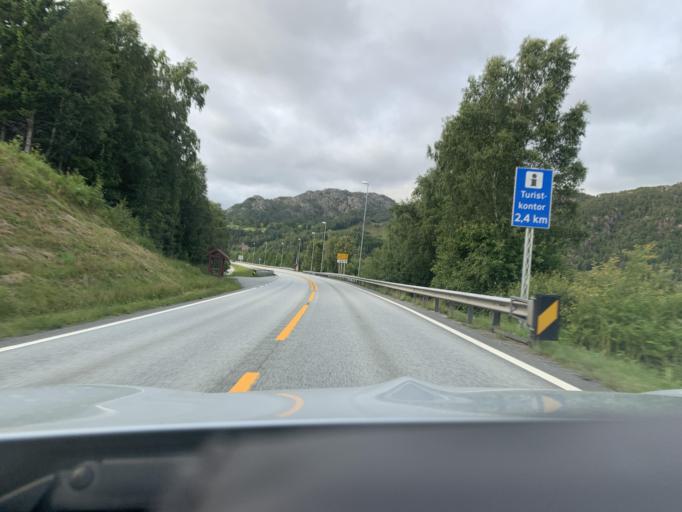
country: NO
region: Rogaland
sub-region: Bjerkreim
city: Vikesa
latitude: 58.6098
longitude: 6.0899
